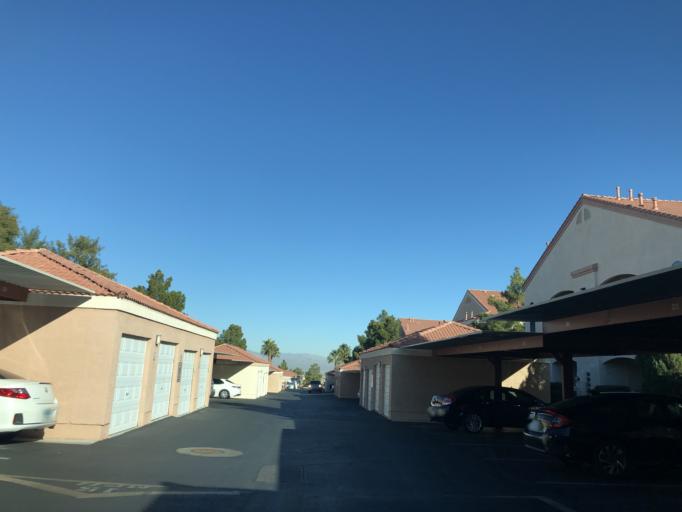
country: US
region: Nevada
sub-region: Clark County
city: Whitney
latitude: 36.0033
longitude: -115.0929
